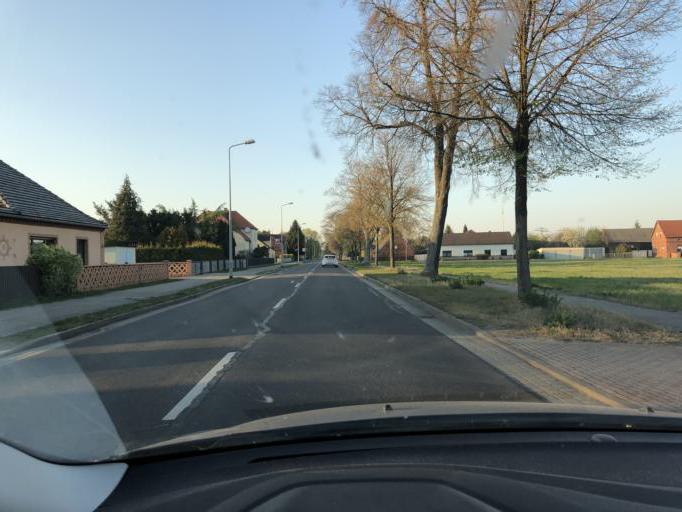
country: DE
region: Brandenburg
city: Spremberg
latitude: 51.5398
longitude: 14.3426
